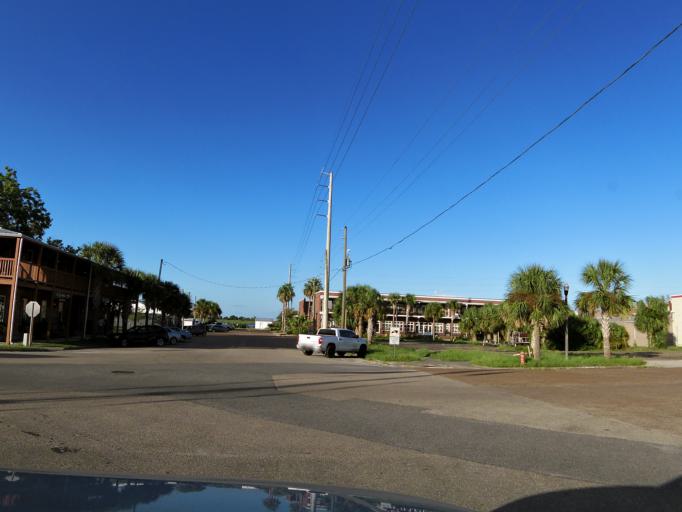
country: US
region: Florida
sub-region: Franklin County
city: Apalachicola
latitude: 29.7284
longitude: -84.9857
